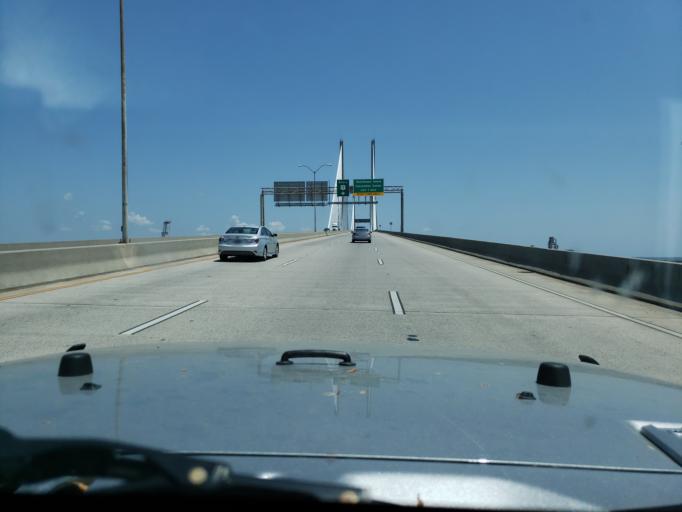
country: US
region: Georgia
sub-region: Chatham County
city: Savannah
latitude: 32.0842
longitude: -81.1025
